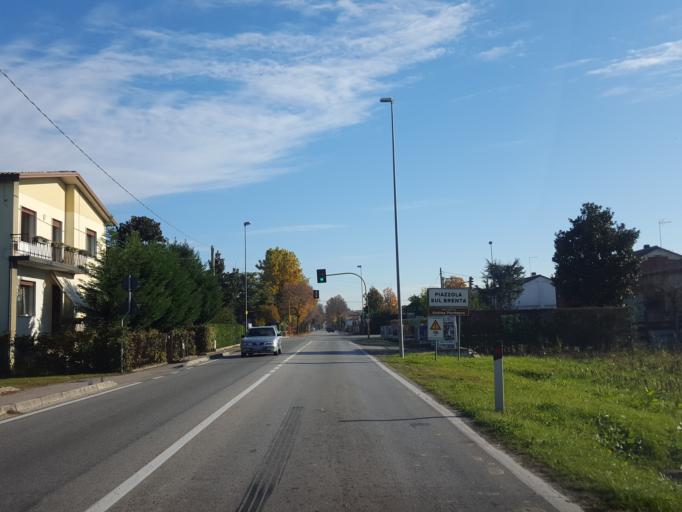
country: IT
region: Veneto
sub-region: Provincia di Padova
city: Piazzola sul Brenta
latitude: 45.5407
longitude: 11.7727
